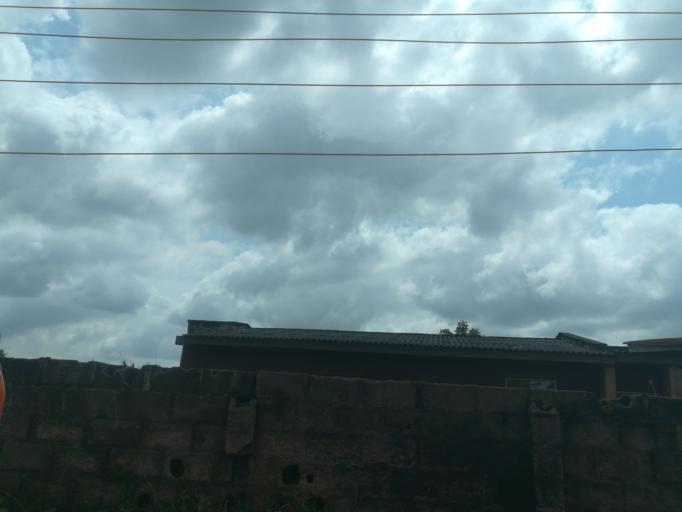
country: NG
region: Oyo
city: Ibadan
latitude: 7.3682
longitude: 3.8238
